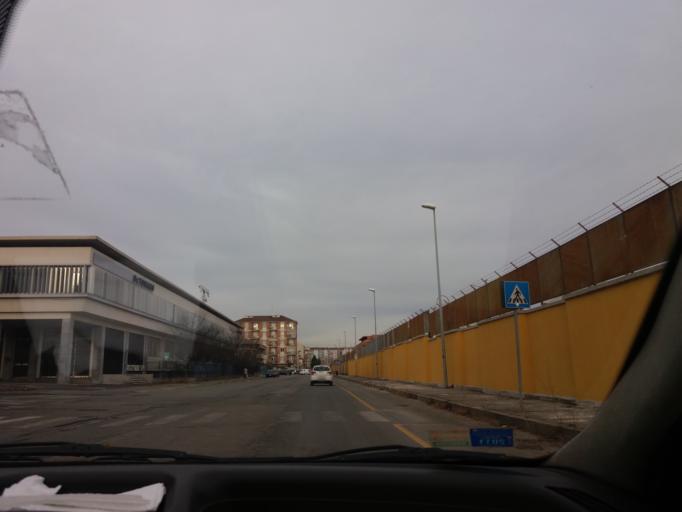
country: IT
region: Piedmont
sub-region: Provincia di Torino
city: Lesna
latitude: 45.0535
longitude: 7.6236
